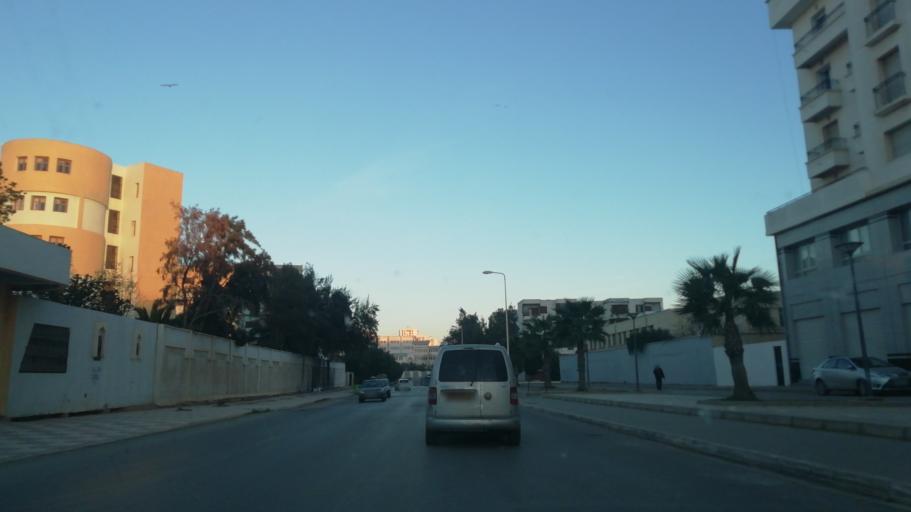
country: DZ
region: Oran
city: Bir el Djir
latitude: 35.6984
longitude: -0.5890
